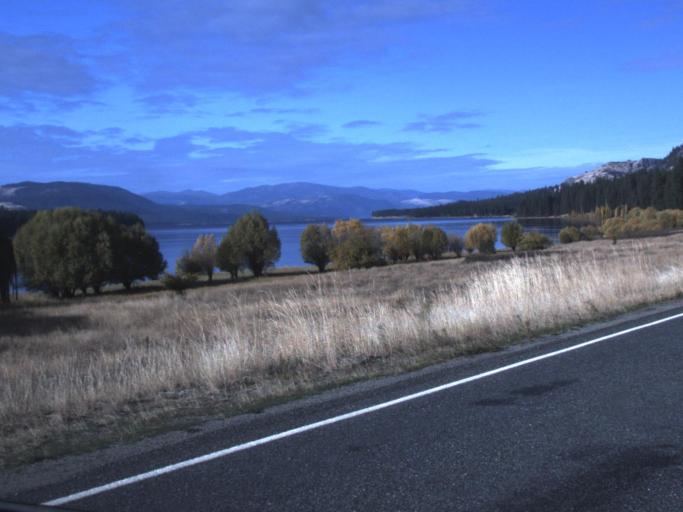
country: US
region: Washington
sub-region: Stevens County
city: Kettle Falls
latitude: 48.2566
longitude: -118.1326
